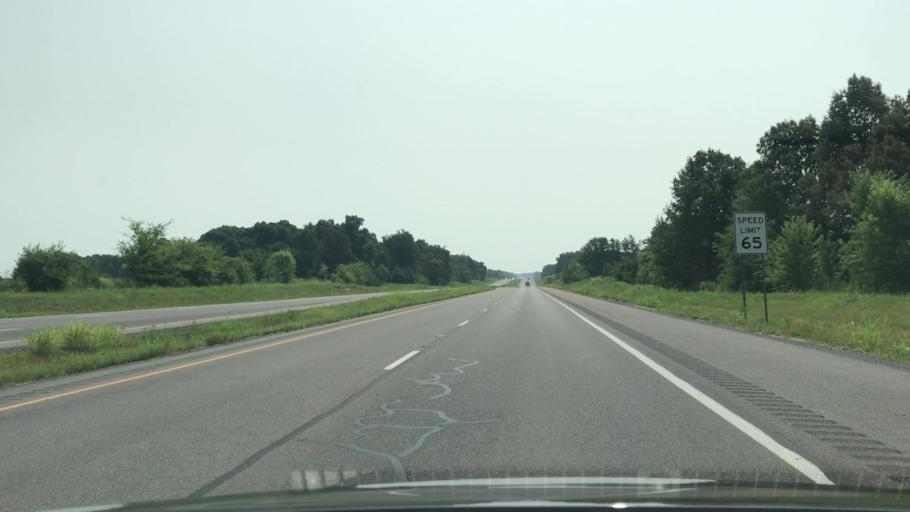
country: US
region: Kentucky
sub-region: Graves County
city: Mayfield
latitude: 36.6744
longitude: -88.5138
